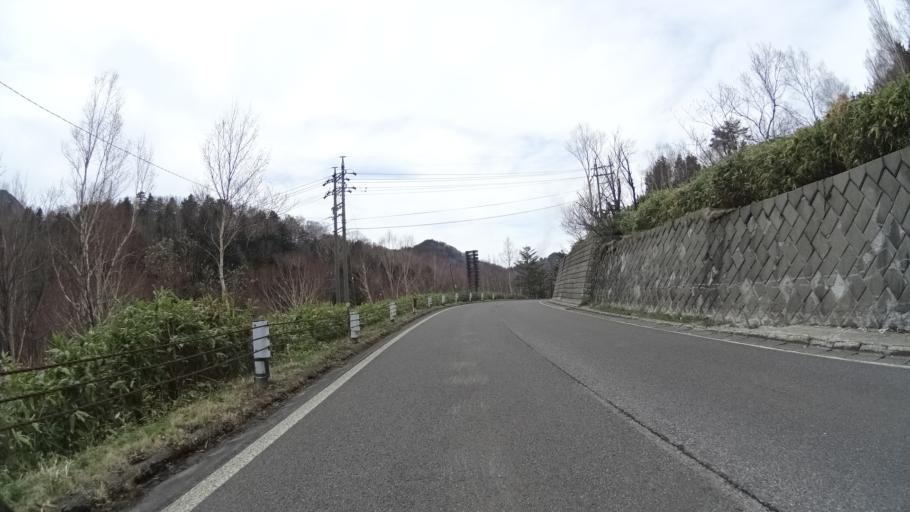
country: JP
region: Nagano
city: Nakano
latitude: 36.6867
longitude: 138.4964
